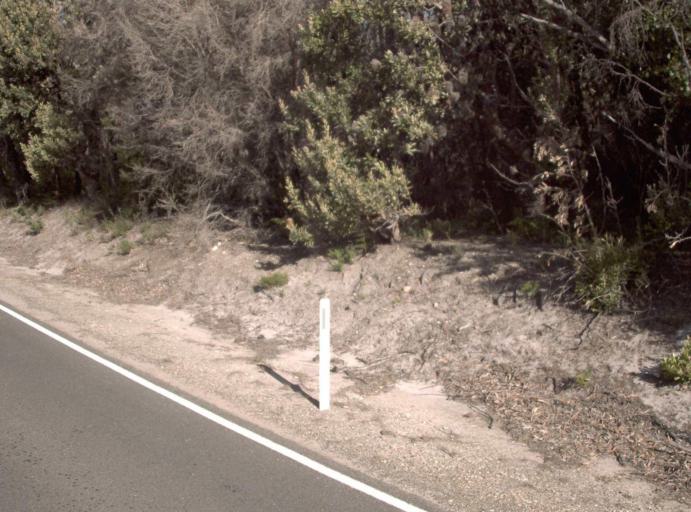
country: AU
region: Victoria
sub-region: East Gippsland
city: Lakes Entrance
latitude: -37.8012
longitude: 148.7300
